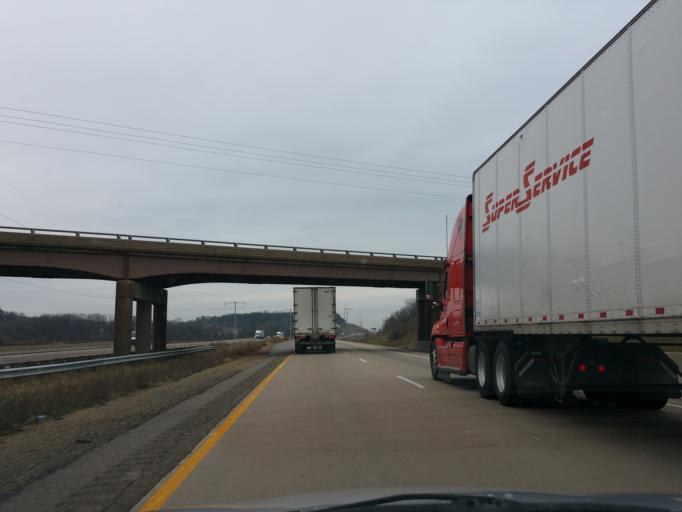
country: US
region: Wisconsin
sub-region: Dane County
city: McFarland
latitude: 43.0207
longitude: -89.2464
